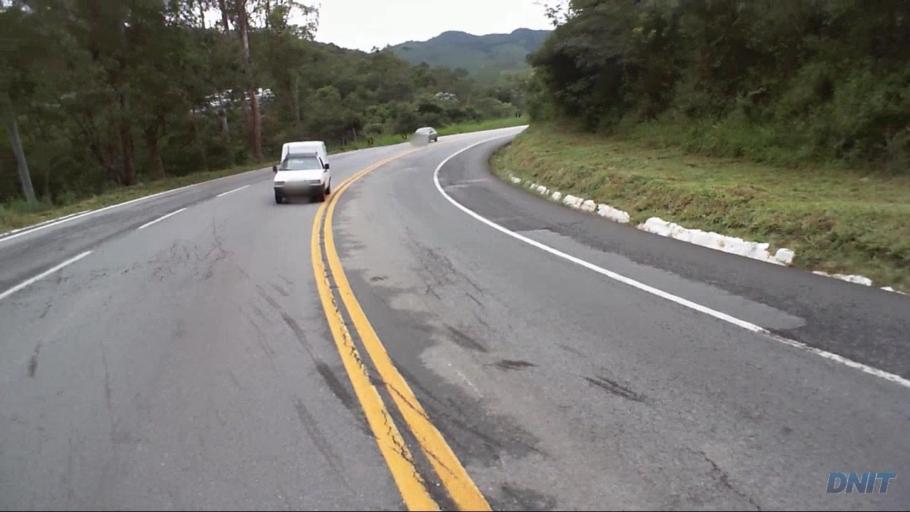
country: BR
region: Minas Gerais
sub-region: Joao Monlevade
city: Joao Monlevade
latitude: -19.8502
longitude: -43.2684
